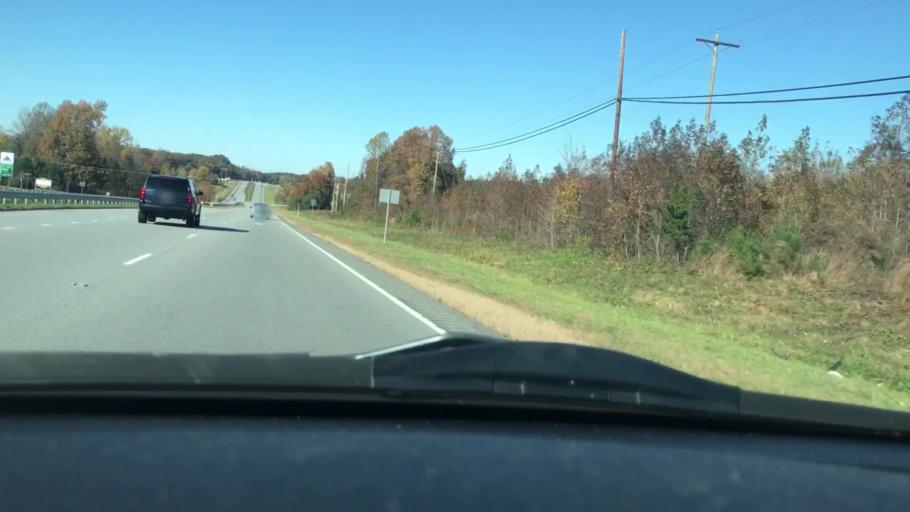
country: US
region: North Carolina
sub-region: Rockingham County
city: Madison
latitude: 36.3160
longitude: -79.9432
